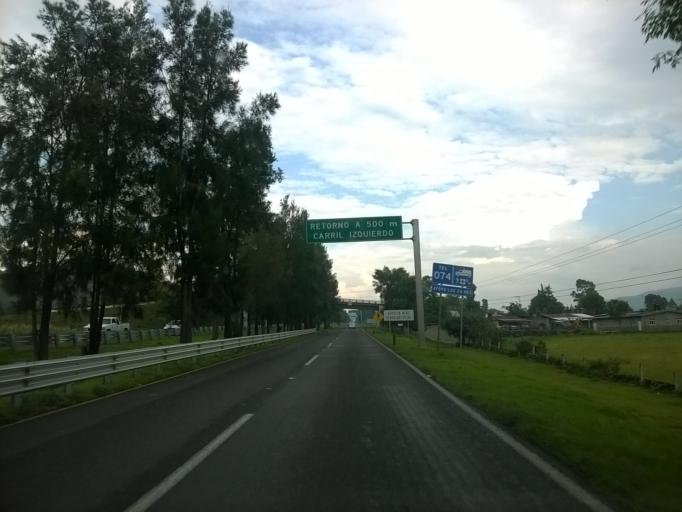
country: MX
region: Michoacan
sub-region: Huiramba
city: El Pedregal
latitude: 19.5323
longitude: -101.4929
